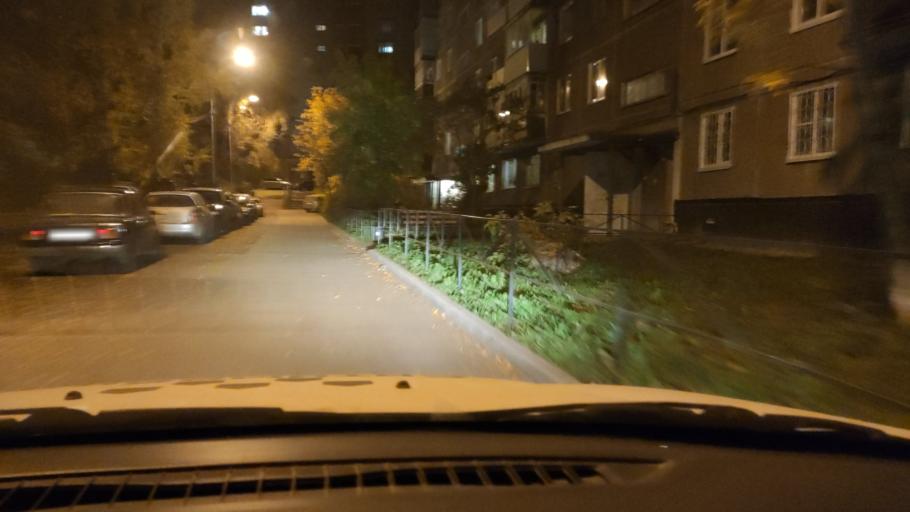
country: RU
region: Perm
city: Perm
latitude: 57.9756
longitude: 56.2398
